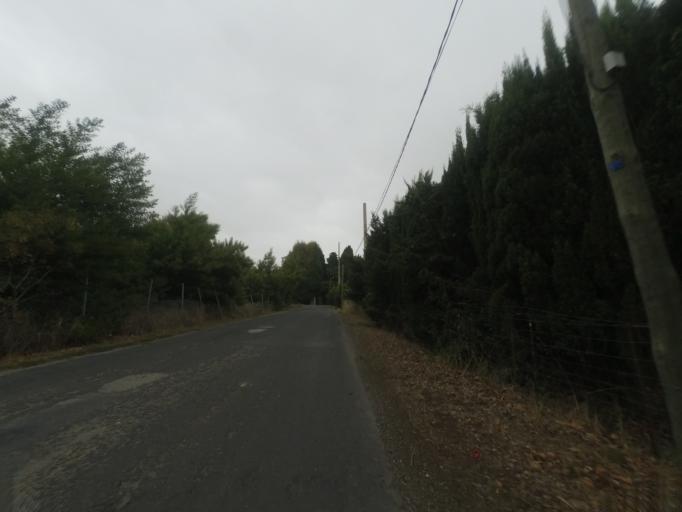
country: FR
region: Languedoc-Roussillon
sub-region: Departement des Pyrenees-Orientales
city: Saint-Esteve
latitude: 42.7054
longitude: 2.8544
